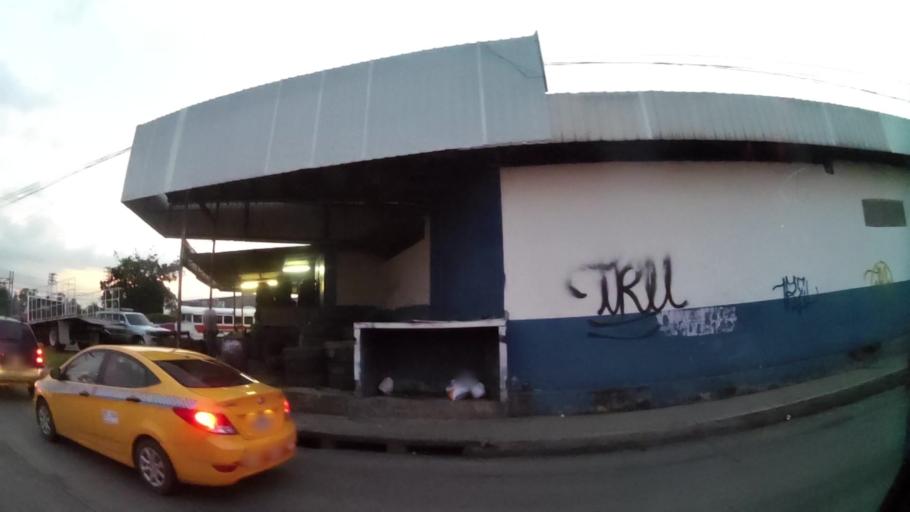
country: PA
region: Panama
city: Tocumen
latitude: 9.0832
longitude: -79.3980
